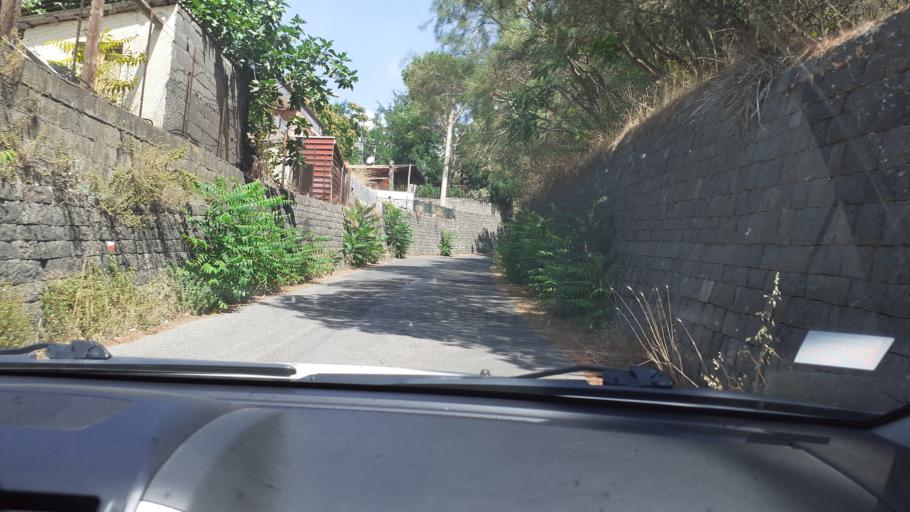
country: IT
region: Sicily
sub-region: Catania
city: Nicolosi
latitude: 37.6286
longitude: 15.0242
